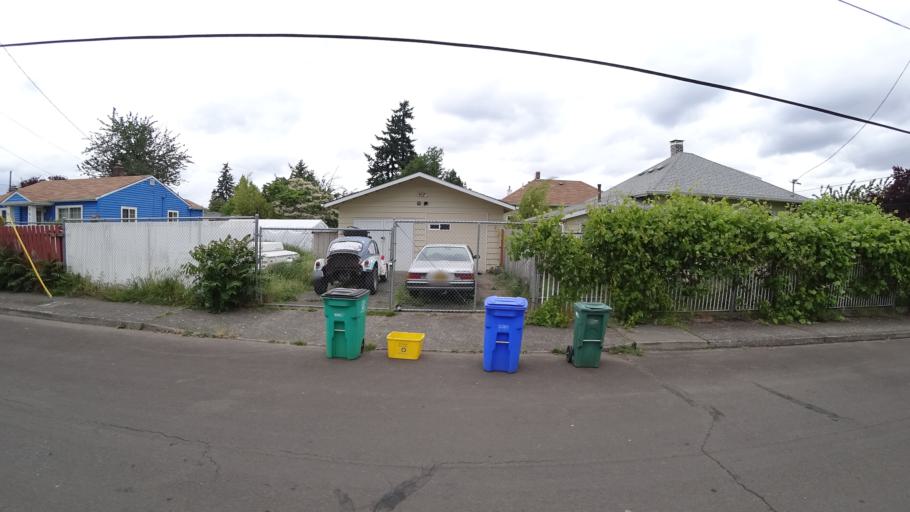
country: US
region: Oregon
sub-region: Multnomah County
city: Lents
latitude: 45.4740
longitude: -122.5763
